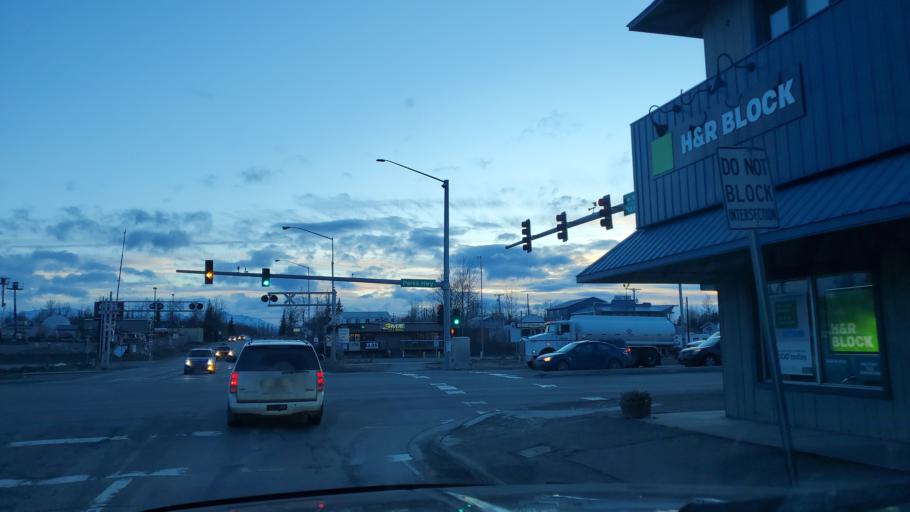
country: US
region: Alaska
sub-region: Matanuska-Susitna Borough
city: Wasilla
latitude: 61.5812
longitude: -149.4416
